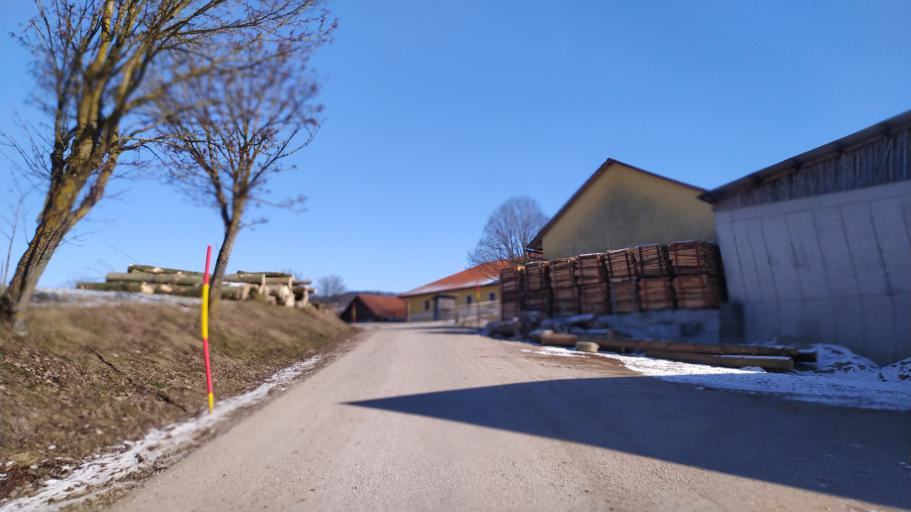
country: AT
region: Upper Austria
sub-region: Politischer Bezirk Urfahr-Umgebung
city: Ottensheim
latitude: 48.3189
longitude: 14.2166
